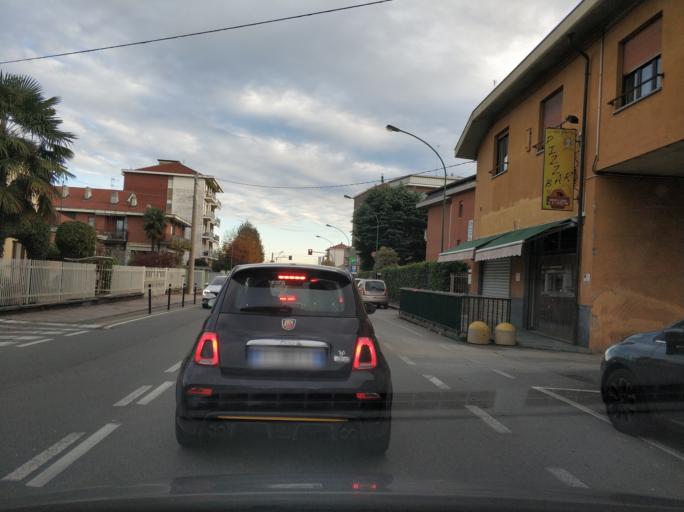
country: IT
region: Piedmont
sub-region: Provincia di Torino
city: Cirie
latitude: 45.2324
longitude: 7.6119
